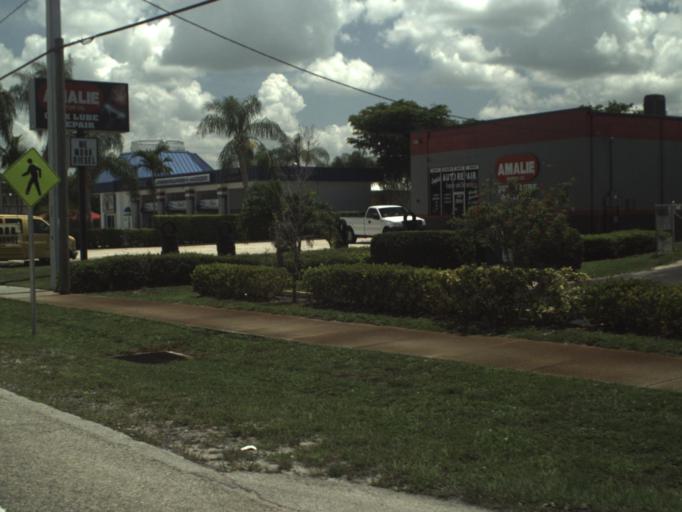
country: US
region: Florida
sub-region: Martin County
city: Port Salerno
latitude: 27.1420
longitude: -80.2123
